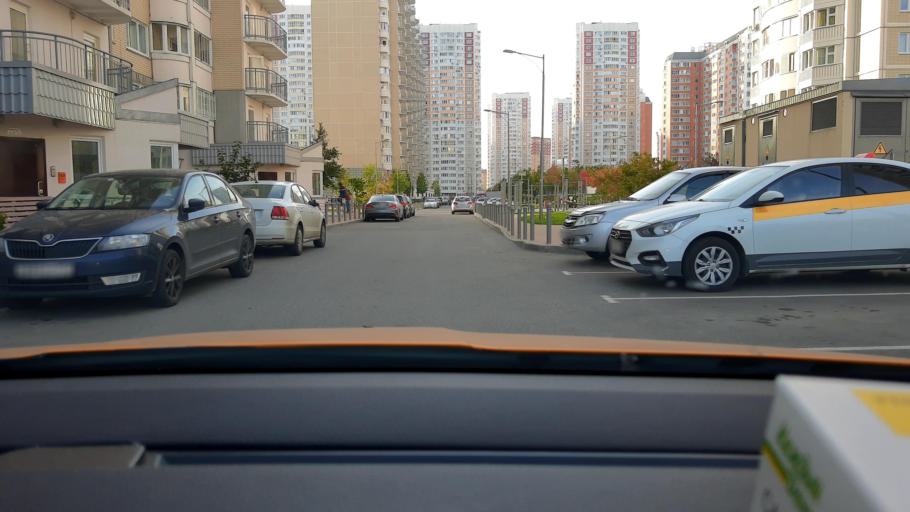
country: RU
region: Moskovskaya
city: Moskovskiy
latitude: 55.6011
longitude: 37.3666
